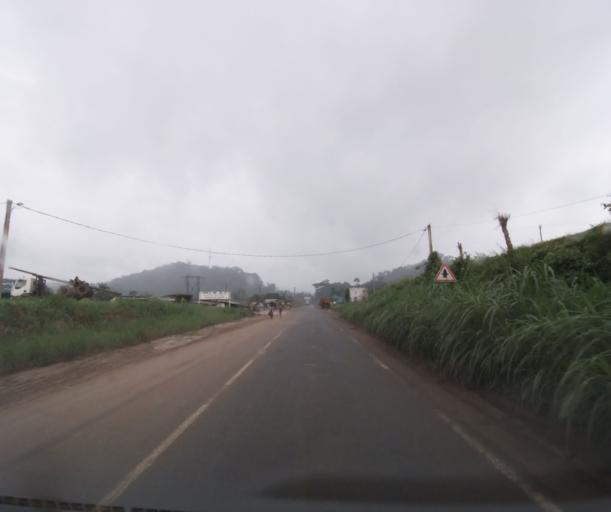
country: CM
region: Centre
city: Eseka
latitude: 3.8894
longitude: 10.7127
